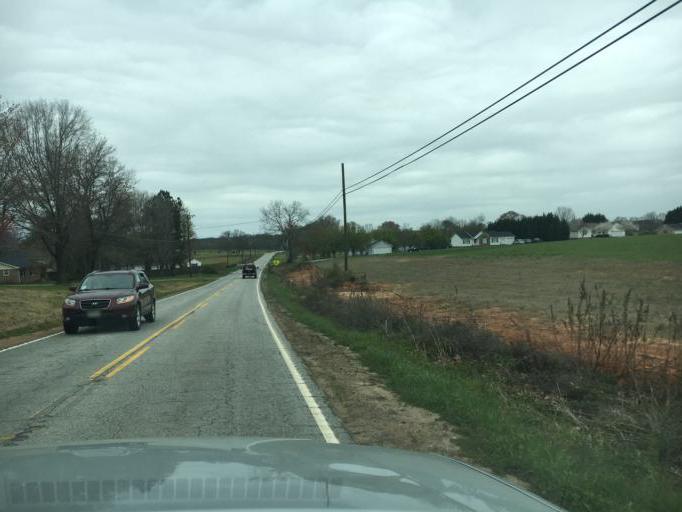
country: US
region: South Carolina
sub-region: Spartanburg County
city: Inman Mills
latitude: 35.0163
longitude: -82.1829
